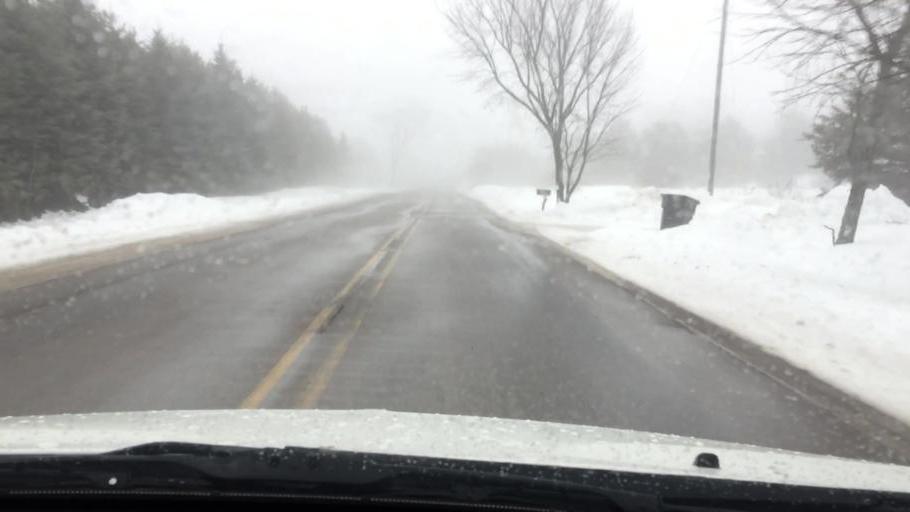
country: US
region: Michigan
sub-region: Charlevoix County
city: East Jordan
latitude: 45.1223
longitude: -85.1801
